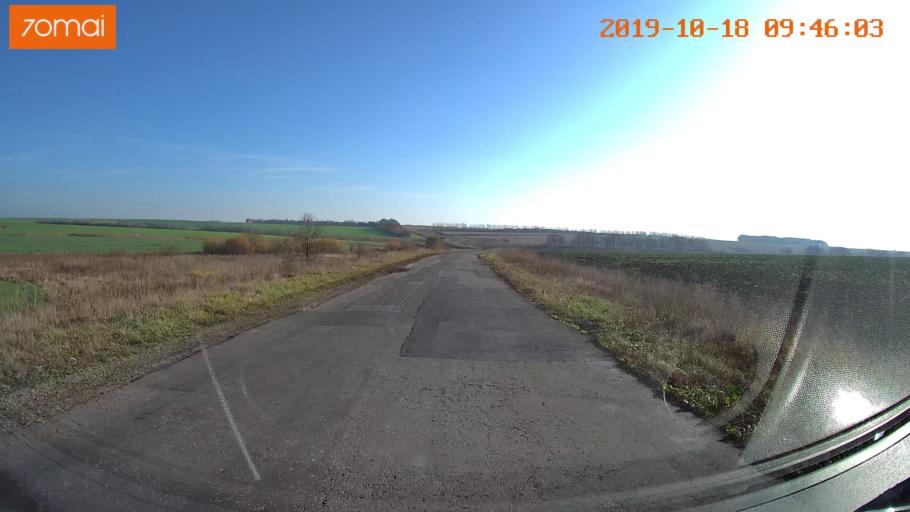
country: RU
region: Tula
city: Kazachka
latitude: 53.3125
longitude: 38.2026
